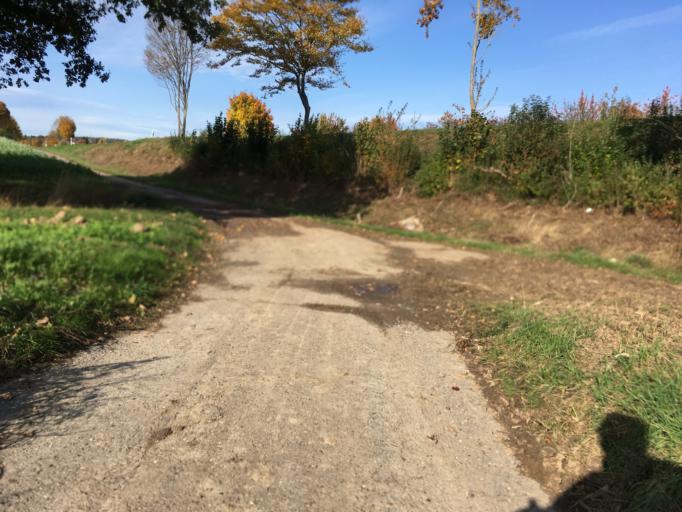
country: DE
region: Baden-Wuerttemberg
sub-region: Regierungsbezirk Stuttgart
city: Siegelsbach
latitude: 49.2498
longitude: 9.0527
